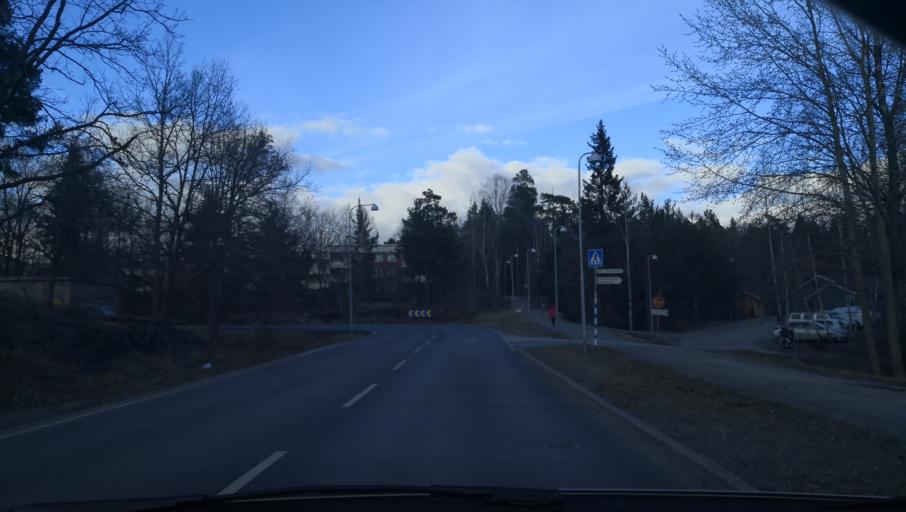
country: SE
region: Stockholm
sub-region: Varmdo Kommun
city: Gustavsberg
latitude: 59.3358
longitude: 18.3945
